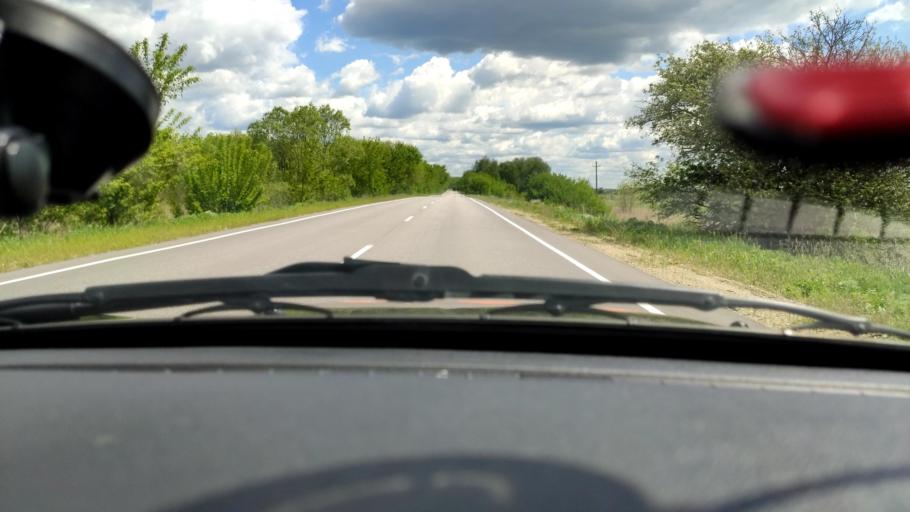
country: RU
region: Belgorod
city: Krasnoye
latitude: 51.0563
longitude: 38.8834
